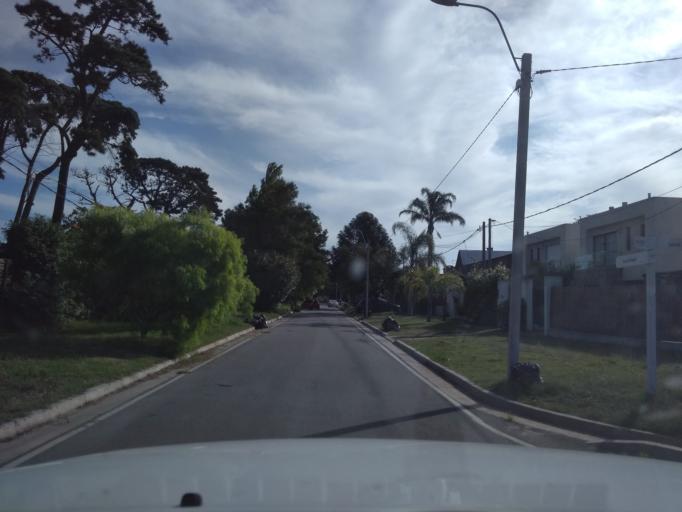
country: UY
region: Canelones
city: Barra de Carrasco
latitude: -34.8695
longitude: -56.0362
